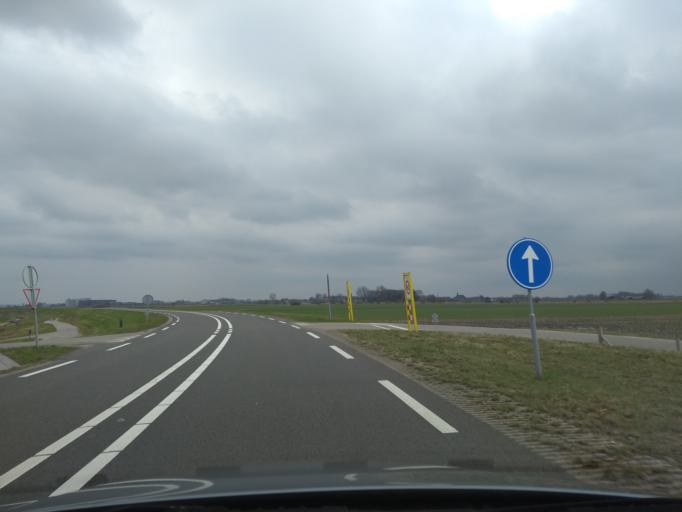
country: NL
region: Overijssel
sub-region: Gemeente Steenwijkerland
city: Sint Jansklooster
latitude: 52.6417
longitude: 6.0244
